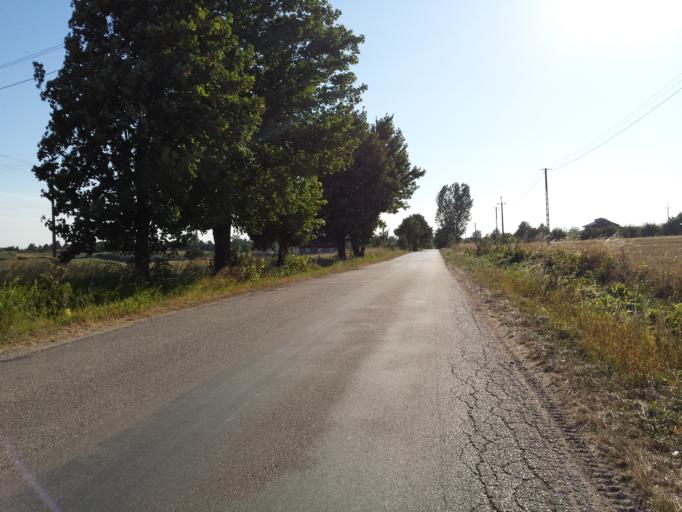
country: PL
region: Swietokrzyskie
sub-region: Powiat buski
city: Gnojno
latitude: 50.6552
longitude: 20.8315
